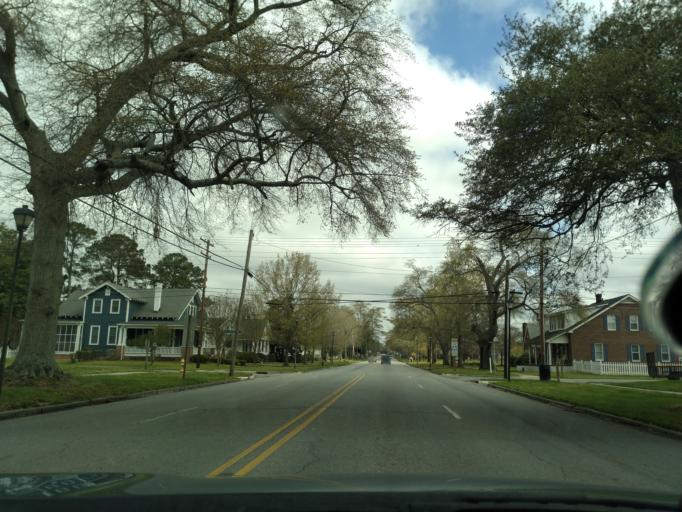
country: US
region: North Carolina
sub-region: Chowan County
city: Edenton
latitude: 36.0647
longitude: -76.6070
